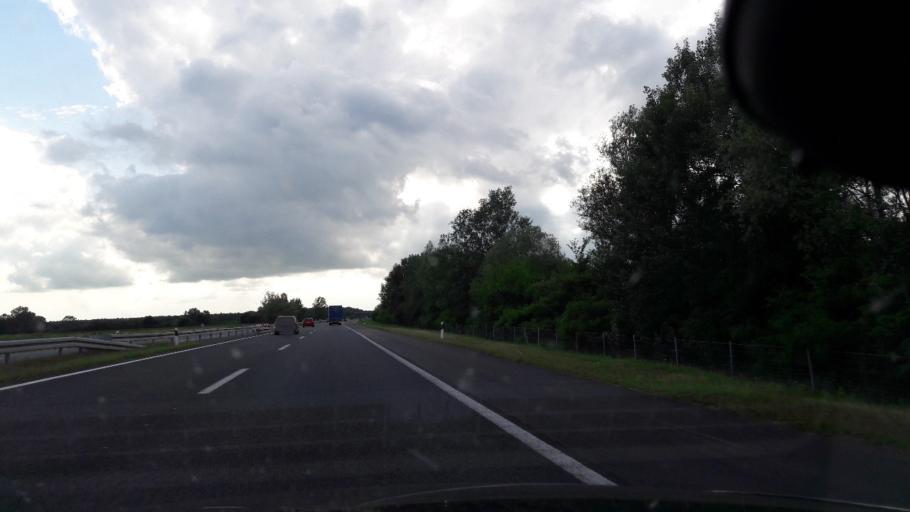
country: HR
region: Brodsko-Posavska
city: Garcin
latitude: 45.1548
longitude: 18.2081
